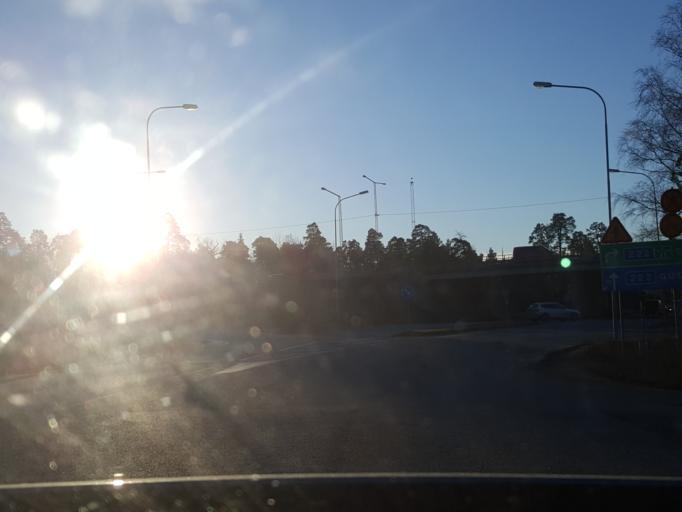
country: SE
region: Stockholm
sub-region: Lidingo
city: Brevik
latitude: 59.3155
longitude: 18.2144
